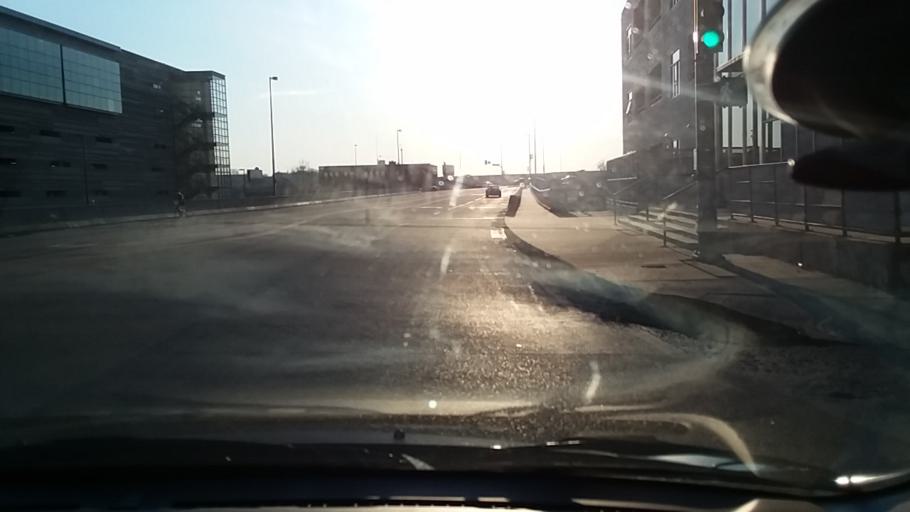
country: US
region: Missouri
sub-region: Jackson County
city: Kansas City
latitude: 39.0834
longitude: -94.5893
